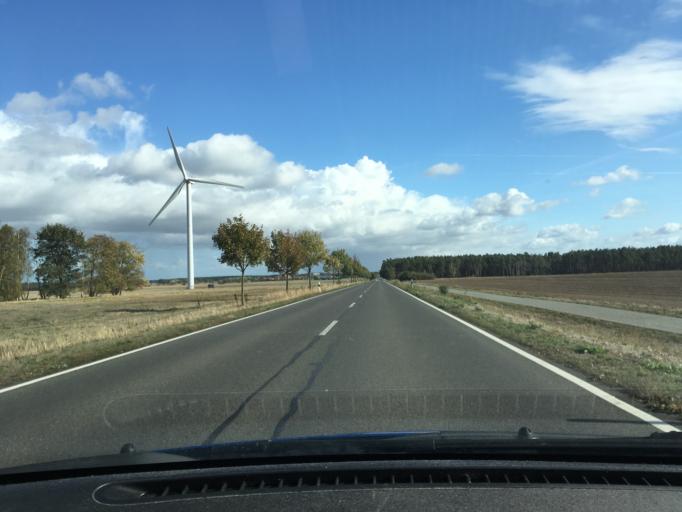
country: DE
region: Saxony-Anhalt
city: Pretzier
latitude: 52.8379
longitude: 11.2312
